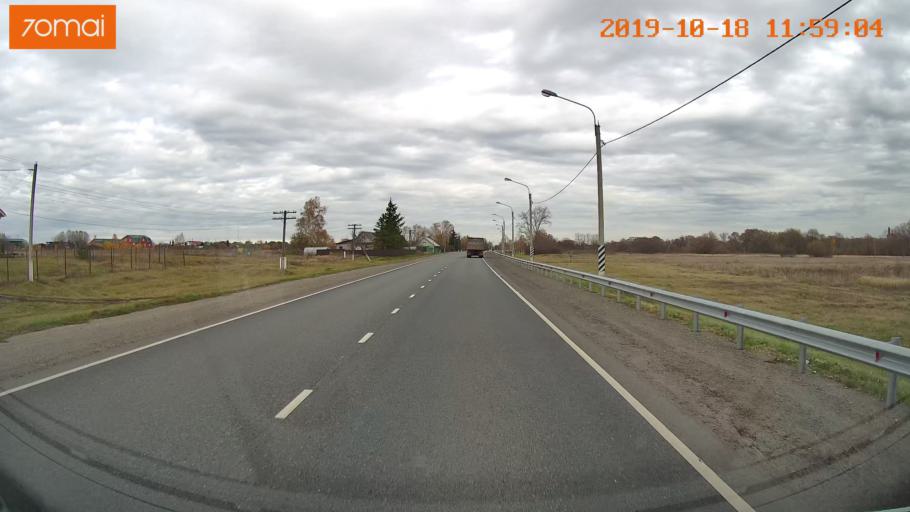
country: RU
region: Rjazan
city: Zakharovo
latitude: 54.2781
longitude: 39.1723
